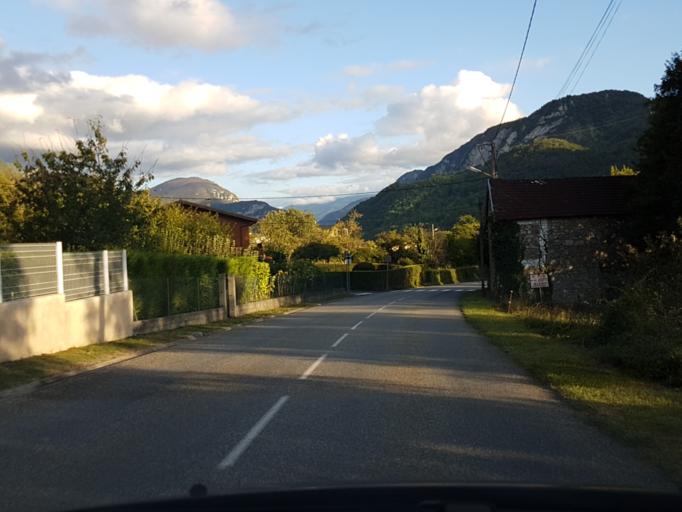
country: FR
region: Midi-Pyrenees
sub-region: Departement de l'Ariege
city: Tarascon-sur-Ariege
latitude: 42.8606
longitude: 1.5754
